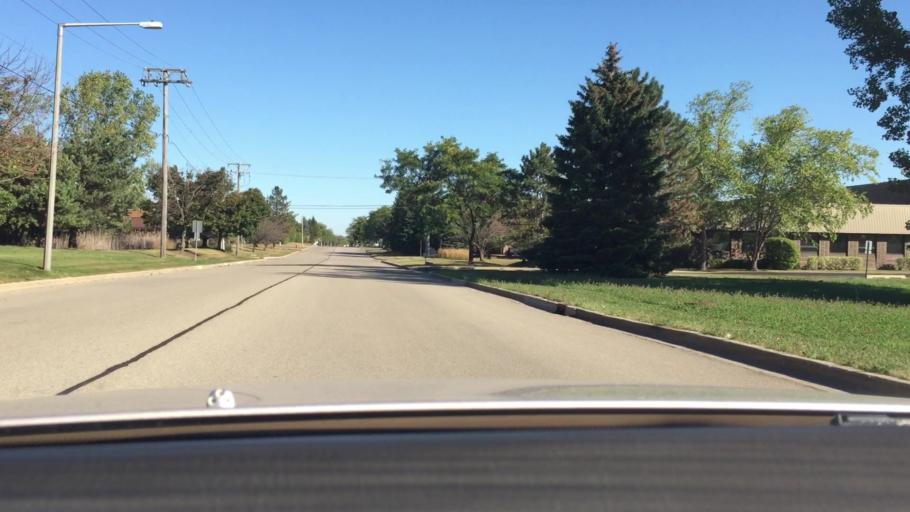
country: US
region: Illinois
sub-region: Lake County
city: Forest Lake
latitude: 42.2037
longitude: -88.0676
